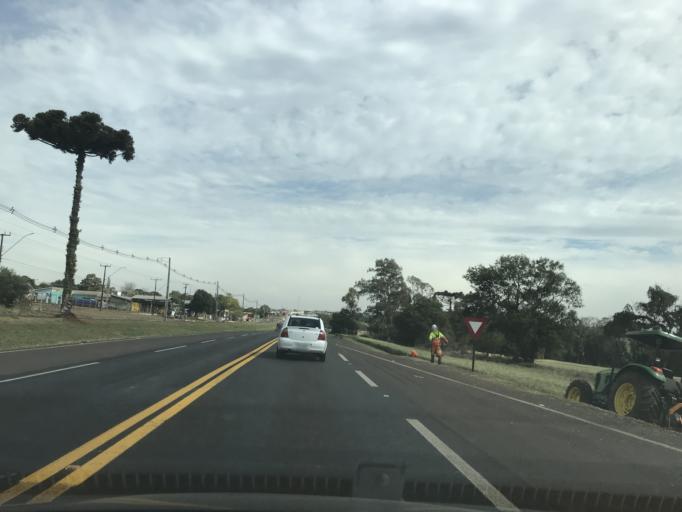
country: BR
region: Parana
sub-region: Cascavel
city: Cascavel
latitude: -25.0434
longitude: -53.6055
